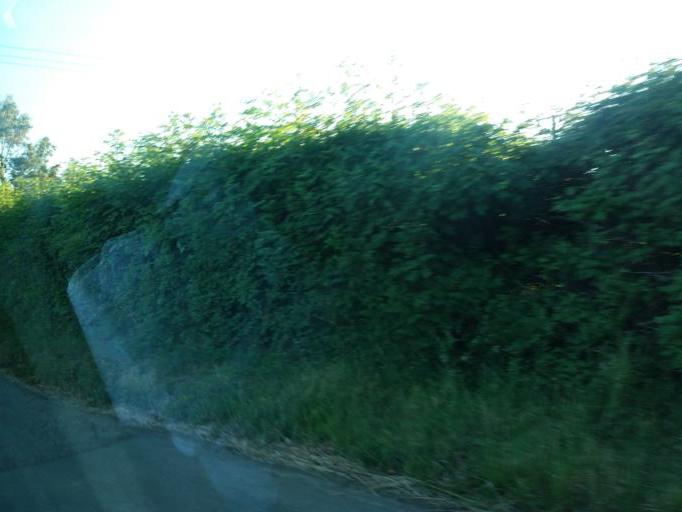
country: IE
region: Leinster
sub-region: An Mhi
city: Ashbourne
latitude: 53.5472
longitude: -6.3591
